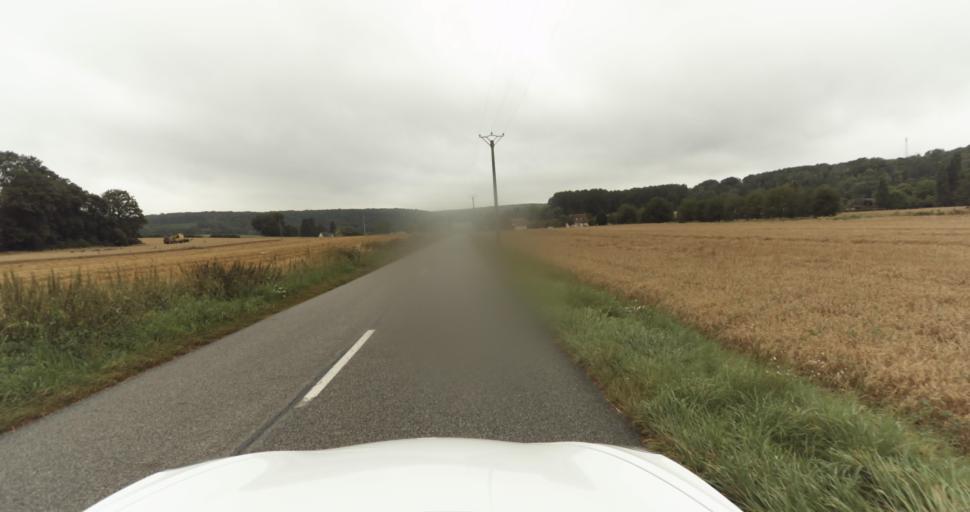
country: FR
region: Haute-Normandie
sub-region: Departement de l'Eure
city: Normanville
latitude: 49.0971
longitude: 1.1258
